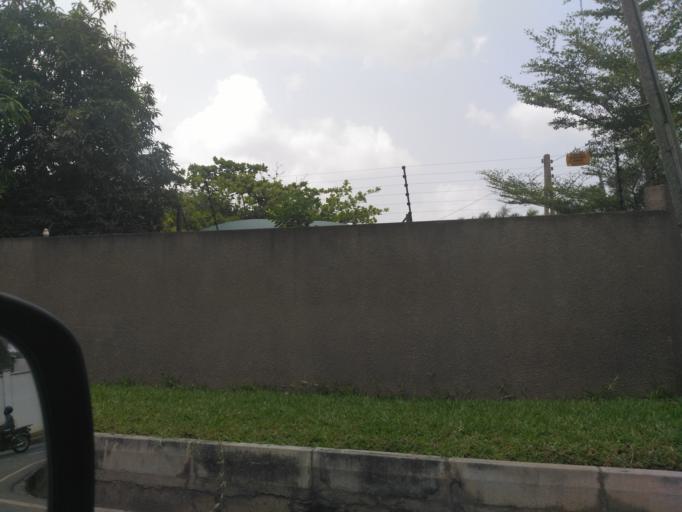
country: GH
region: Greater Accra
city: Accra
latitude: 5.6052
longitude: -0.1806
